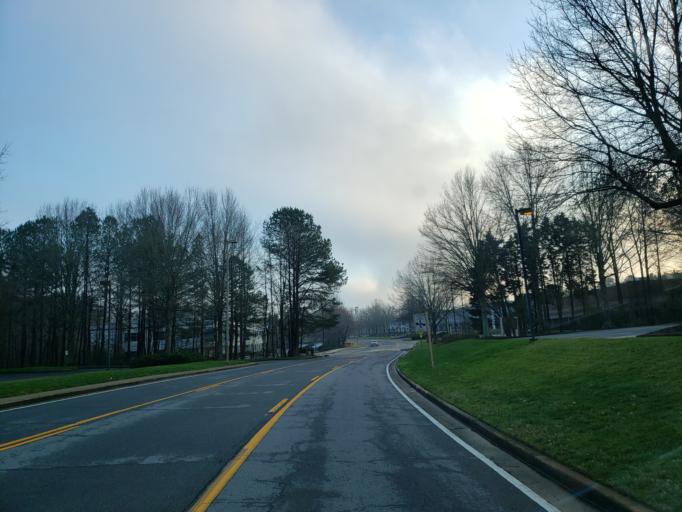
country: US
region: Georgia
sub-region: Cobb County
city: Kennesaw
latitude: 34.0096
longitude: -84.5959
